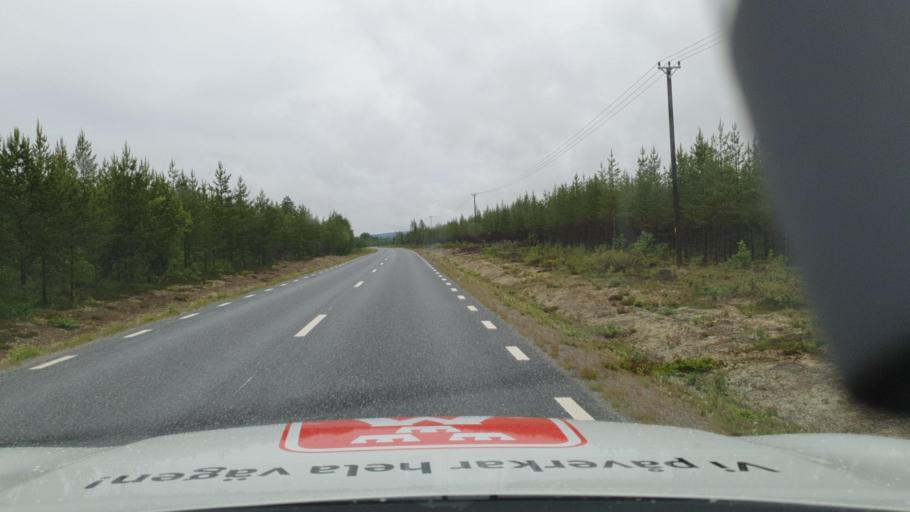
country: SE
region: Vaesterbotten
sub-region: Asele Kommun
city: Asele
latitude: 63.9574
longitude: 17.2704
